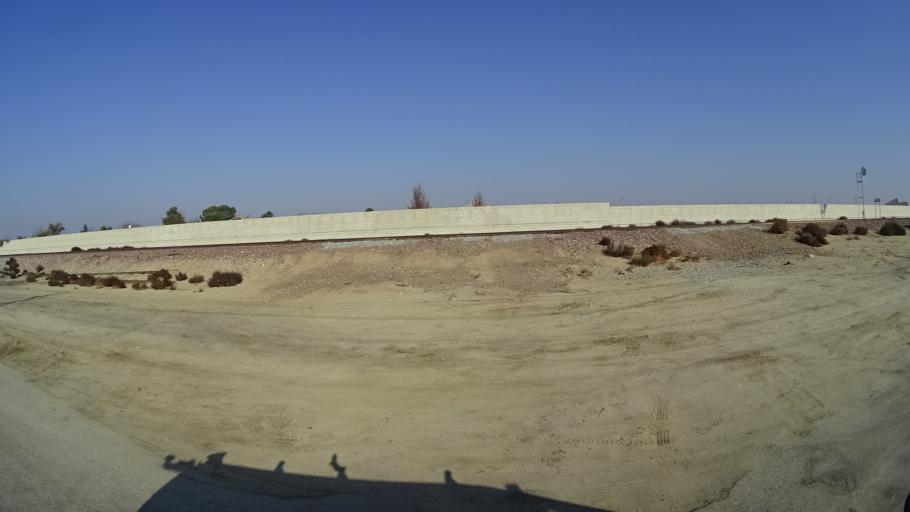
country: US
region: California
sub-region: Kern County
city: Greenacres
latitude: 35.3761
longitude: -119.1060
